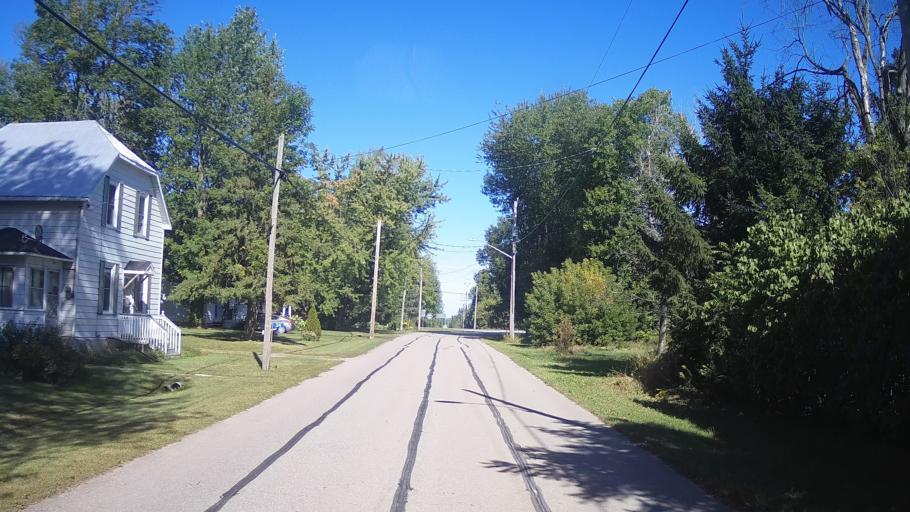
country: CA
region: Ontario
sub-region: Lanark County
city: Smiths Falls
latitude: 44.8395
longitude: -75.8882
